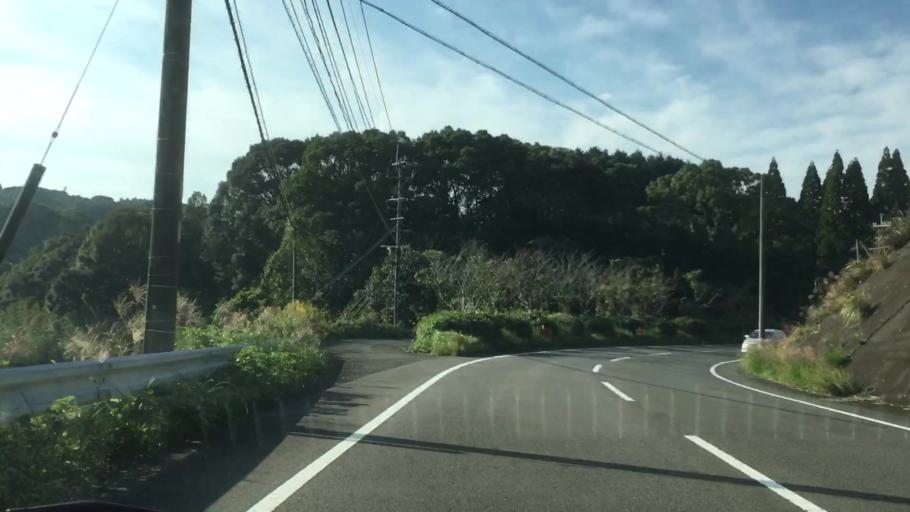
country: JP
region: Nagasaki
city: Sasebo
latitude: 32.9528
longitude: 129.6747
